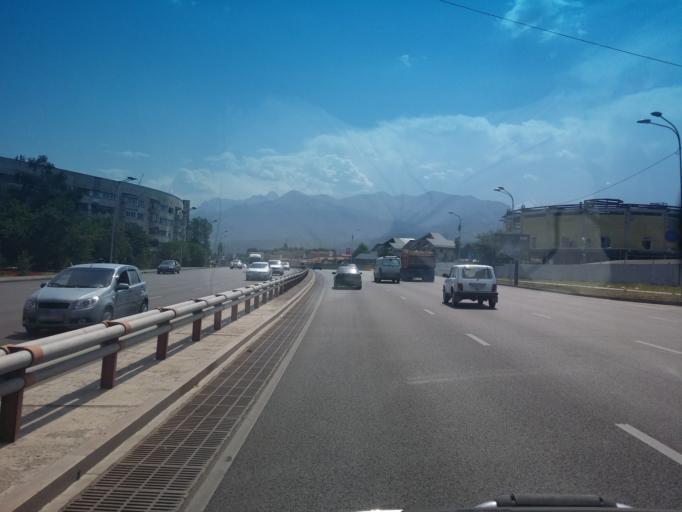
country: KZ
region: Almaty Qalasy
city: Almaty
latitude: 43.1967
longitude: 76.8727
